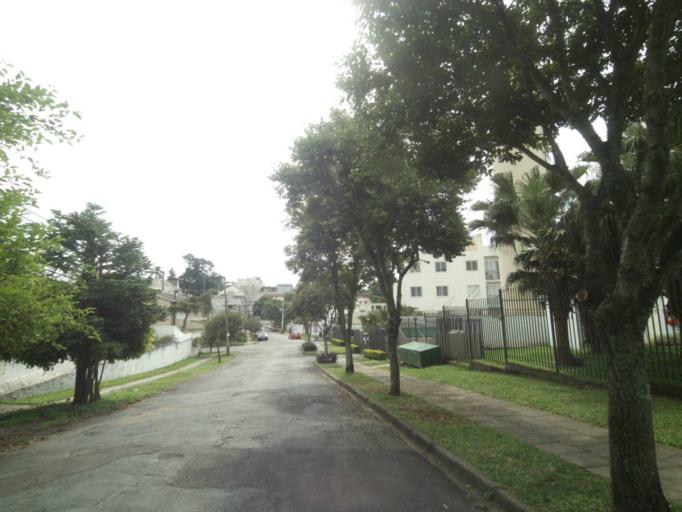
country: BR
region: Parana
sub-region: Curitiba
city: Curitiba
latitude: -25.4079
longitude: -49.2946
